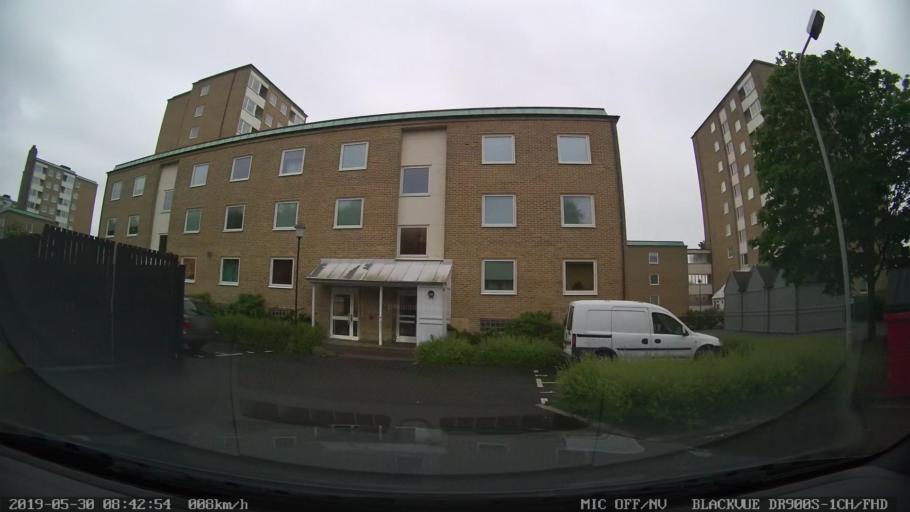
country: SE
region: Skane
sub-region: Landskrona
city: Landskrona
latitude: 55.8837
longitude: 12.8248
